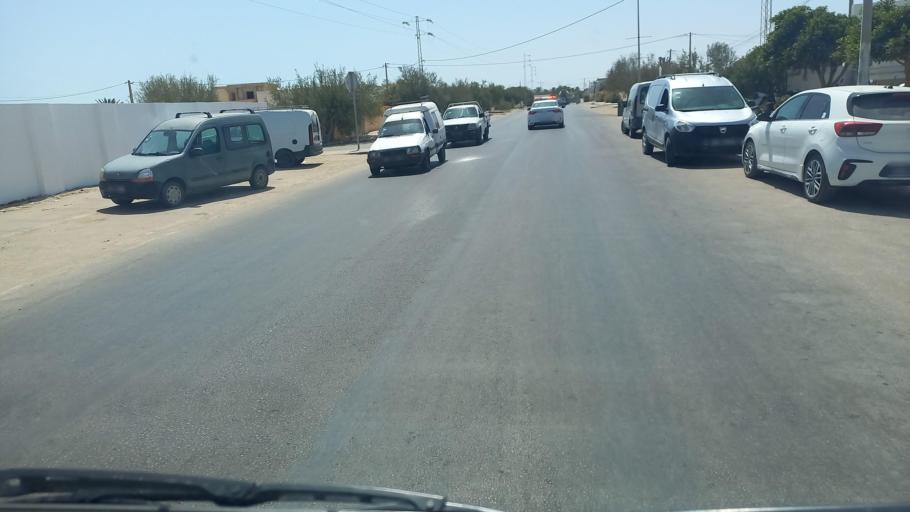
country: TN
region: Madanin
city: Houmt Souk
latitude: 33.7980
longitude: 10.8849
